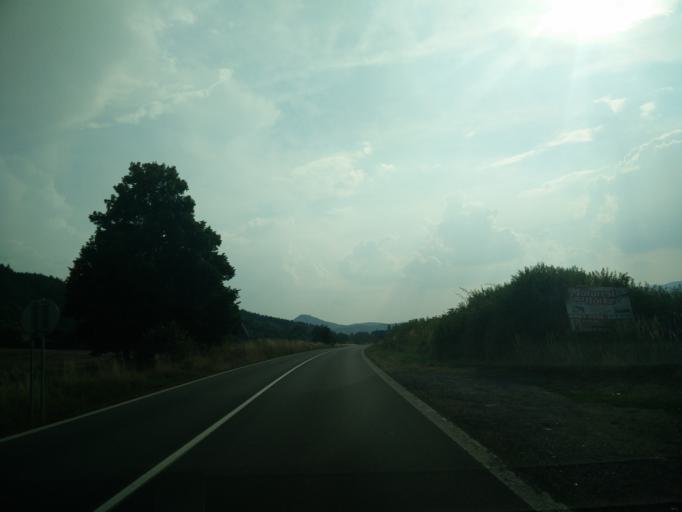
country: SK
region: Banskobystricky
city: Ziar nad Hronom
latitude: 48.5482
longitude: 18.8176
